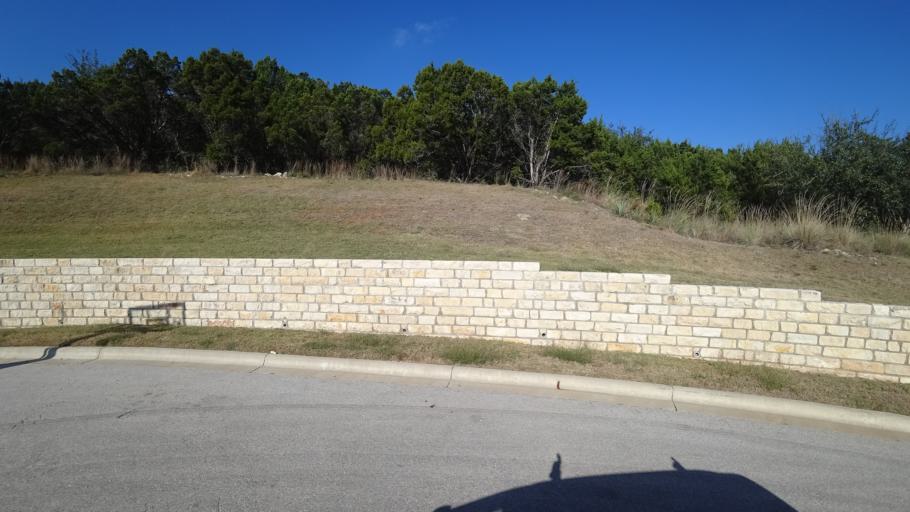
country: US
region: Texas
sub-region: Travis County
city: Bee Cave
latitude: 30.3466
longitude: -97.8919
